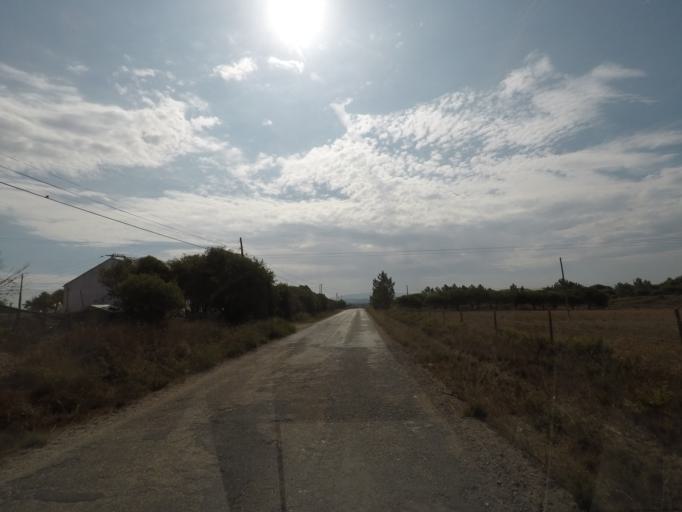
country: PT
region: Beja
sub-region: Odemira
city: Sao Teotonio
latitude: 37.4740
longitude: -8.7583
